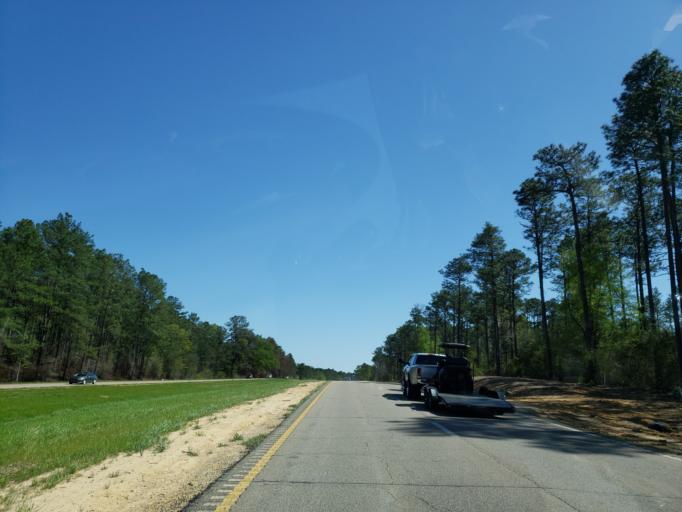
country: US
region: Mississippi
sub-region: Lamar County
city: Purvis
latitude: 31.1098
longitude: -89.2192
